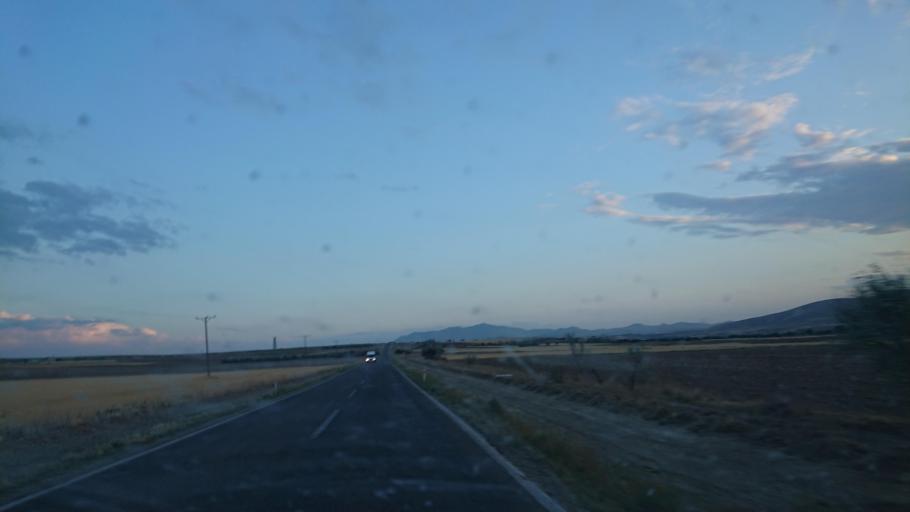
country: TR
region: Aksaray
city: Balci
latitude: 38.8102
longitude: 34.1323
